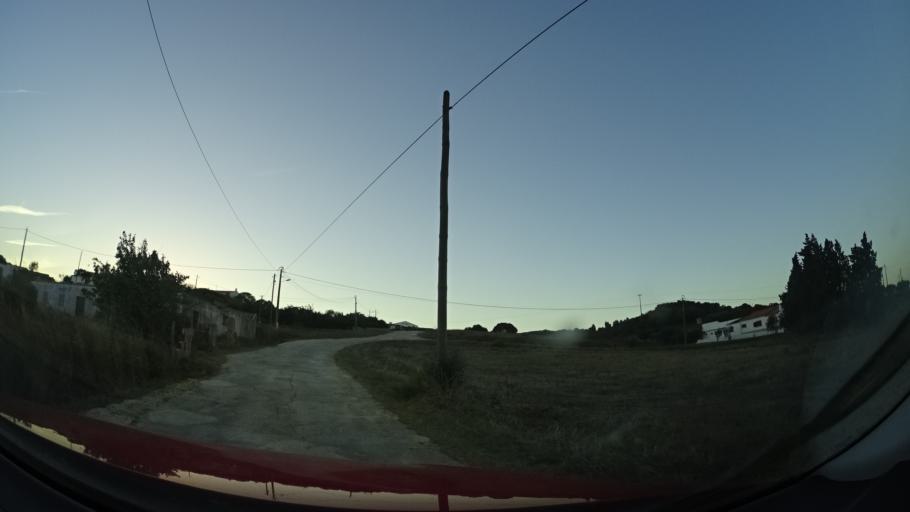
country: PT
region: Faro
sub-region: Aljezur
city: Aljezur
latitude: 37.2383
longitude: -8.8306
